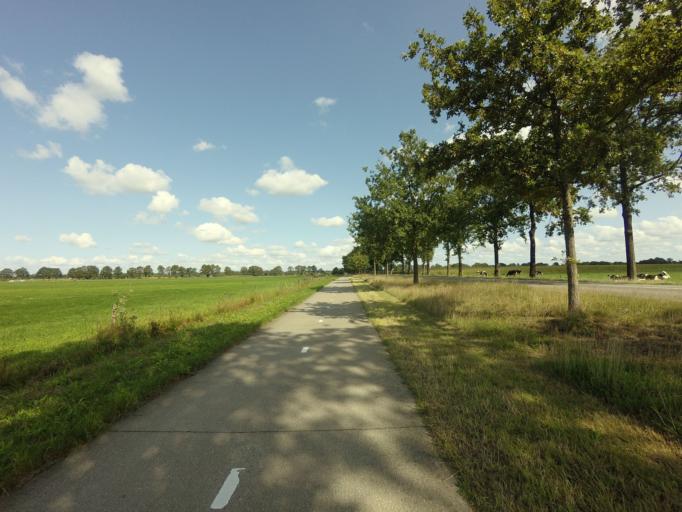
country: NL
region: Overijssel
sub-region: Gemeente Dalfsen
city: Dalfsen
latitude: 52.5524
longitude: 6.2618
